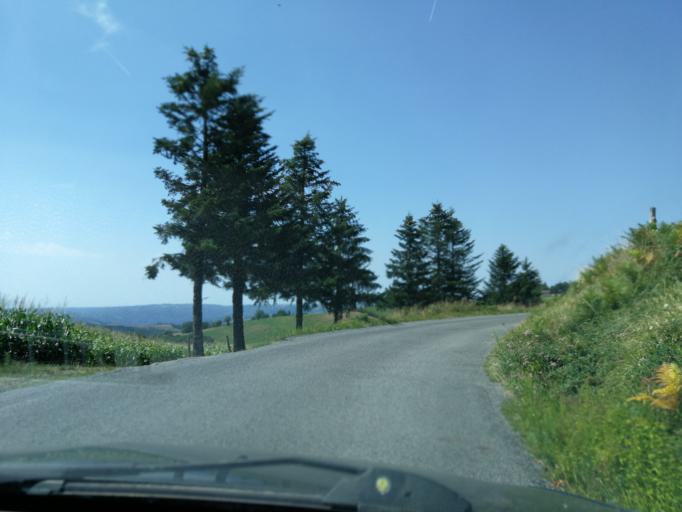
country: FR
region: Midi-Pyrenees
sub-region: Departement de l'Aveyron
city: Livinhac-le-Haut
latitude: 44.6637
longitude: 2.3162
